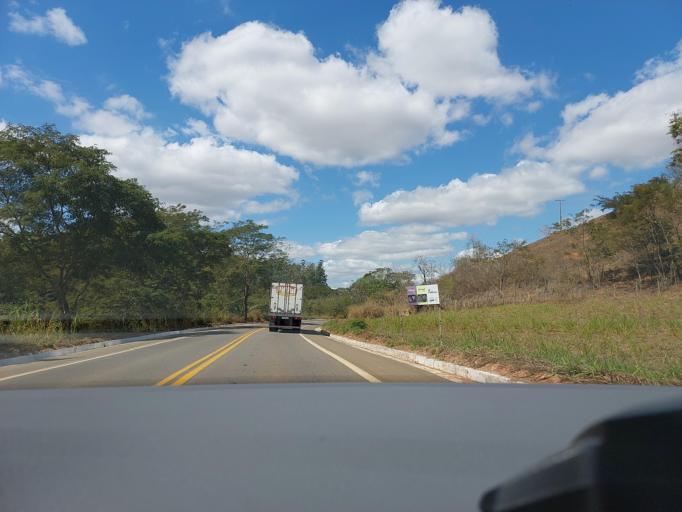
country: BR
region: Minas Gerais
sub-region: Muriae
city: Muriae
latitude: -21.1238
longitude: -42.2059
